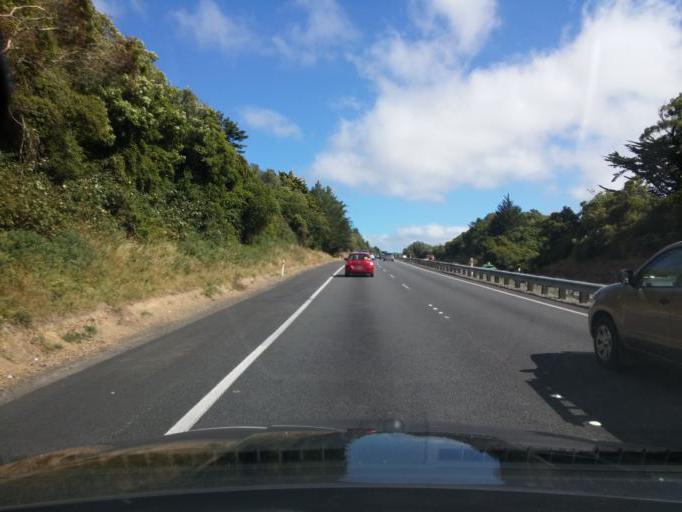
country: NZ
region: Wellington
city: Petone
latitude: -41.2110
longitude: 174.8154
